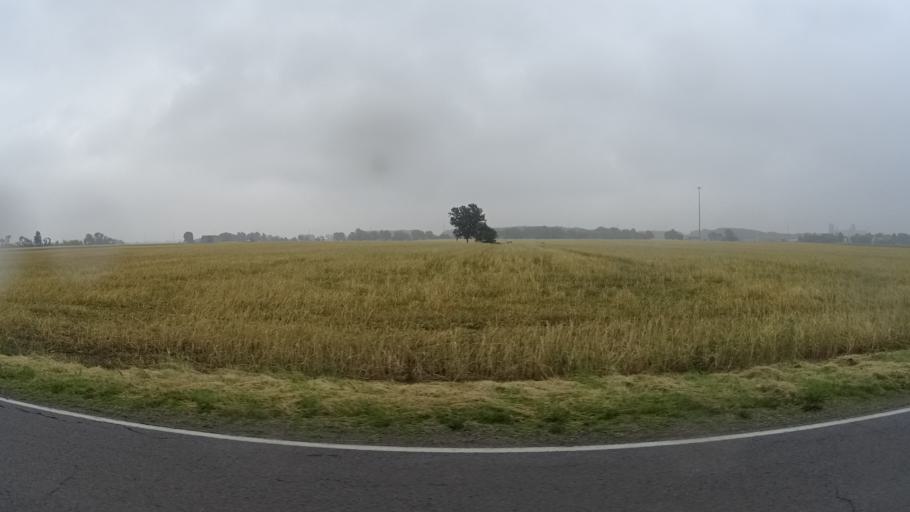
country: US
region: Ohio
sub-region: Huron County
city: Bellevue
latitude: 41.2973
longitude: -82.8418
